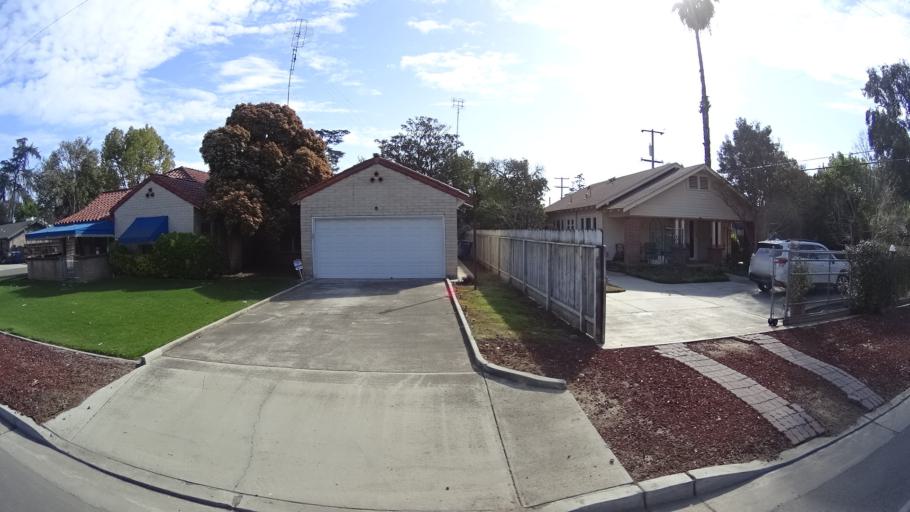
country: US
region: California
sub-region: Fresno County
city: Fresno
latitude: 36.7909
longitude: -119.7996
